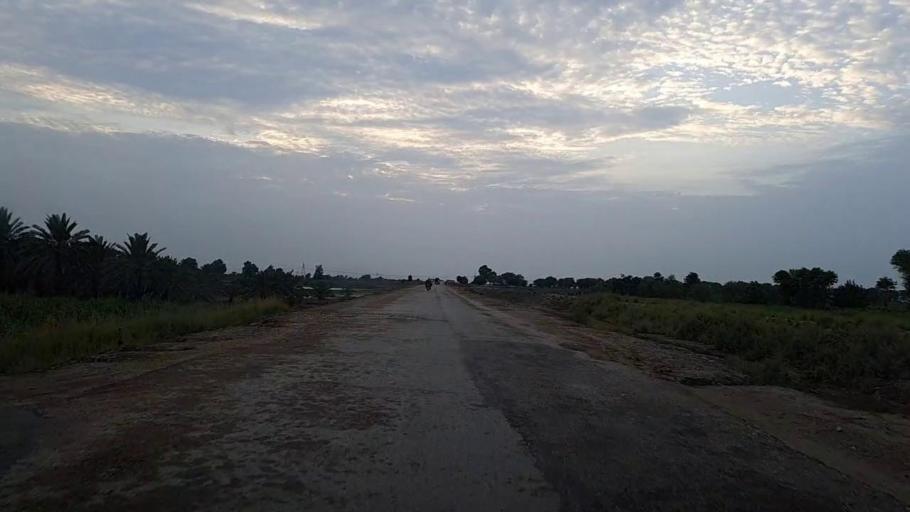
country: PK
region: Sindh
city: Naushahro Firoz
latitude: 26.8221
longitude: 68.1641
